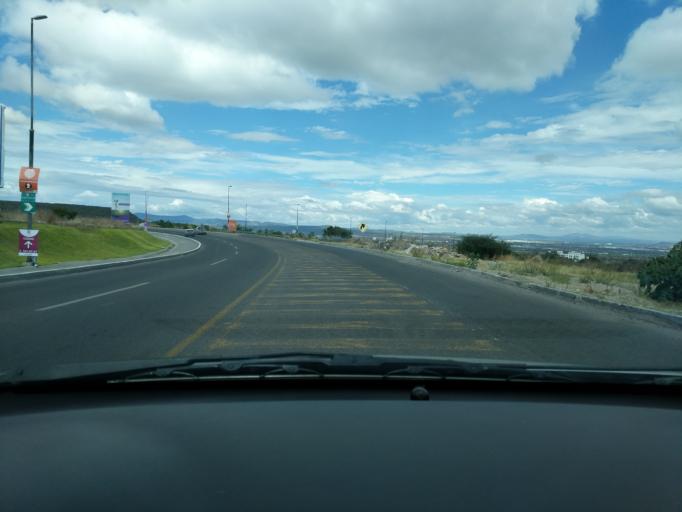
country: MX
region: Queretaro
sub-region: El Marques
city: La Pradera
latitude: 20.6691
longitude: -100.3186
